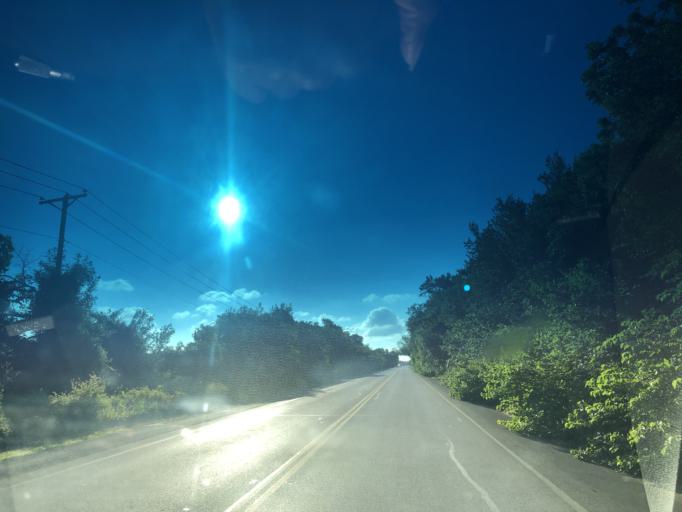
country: US
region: Texas
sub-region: Dallas County
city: Grand Prairie
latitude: 32.7778
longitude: -97.0028
